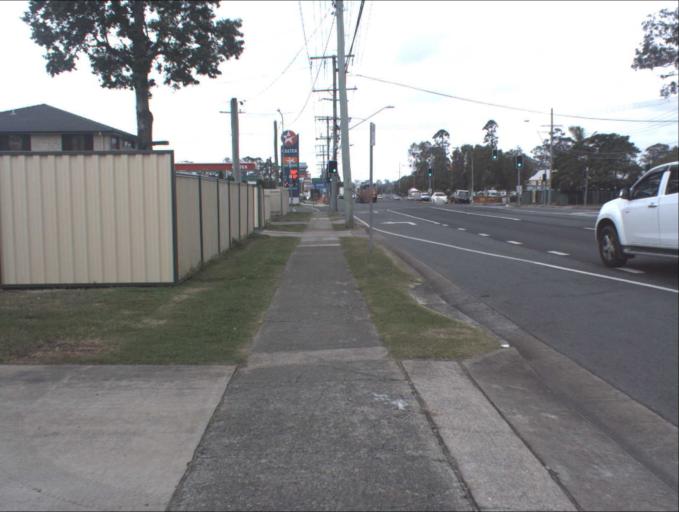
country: AU
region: Queensland
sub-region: Logan
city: Waterford West
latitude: -27.6915
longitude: 153.1332
